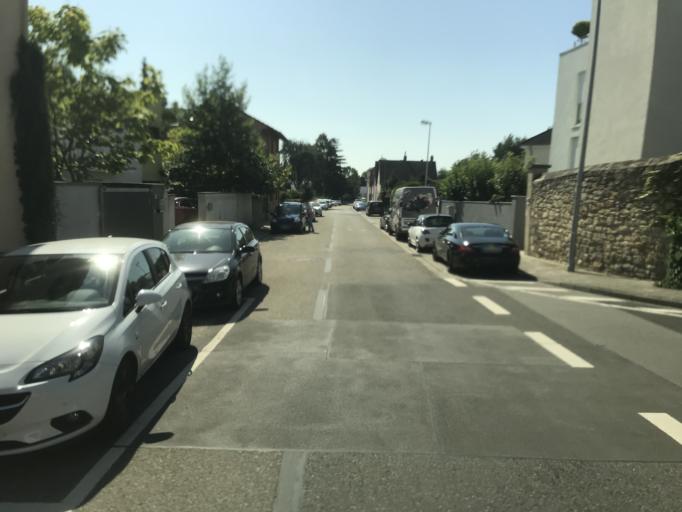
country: DE
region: Rheinland-Pfalz
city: Bodenheim
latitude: 49.9583
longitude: 8.3094
